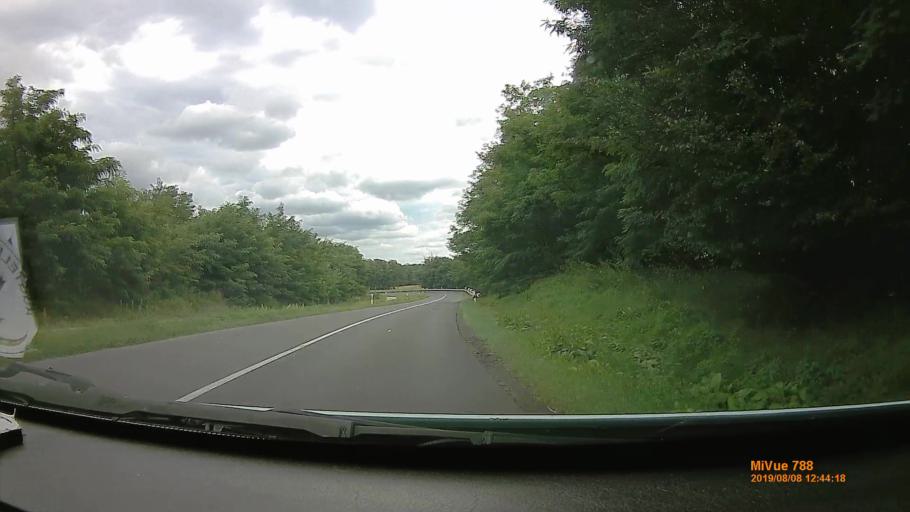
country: HU
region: Szabolcs-Szatmar-Bereg
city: Hodasz
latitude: 47.8830
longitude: 22.1952
